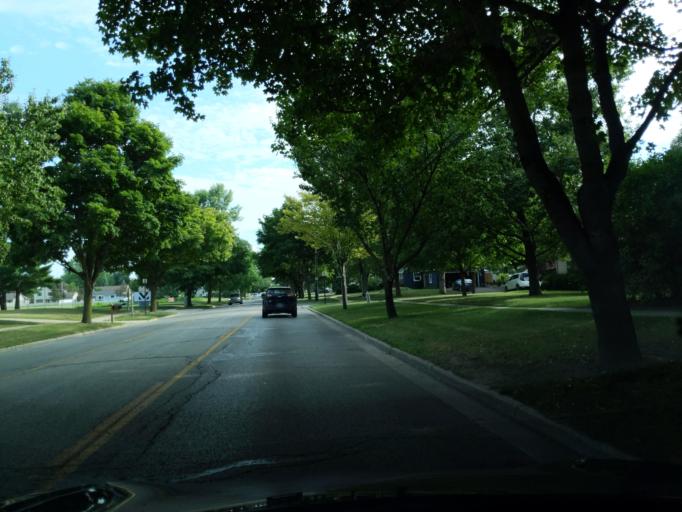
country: US
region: Michigan
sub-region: Midland County
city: Midland
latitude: 43.6504
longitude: -84.2270
